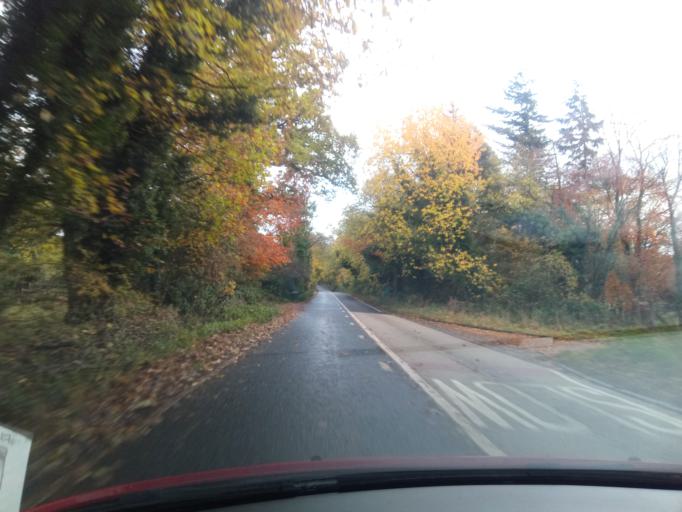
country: GB
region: England
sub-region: Northumberland
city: Wall
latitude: 55.0224
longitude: -2.1196
